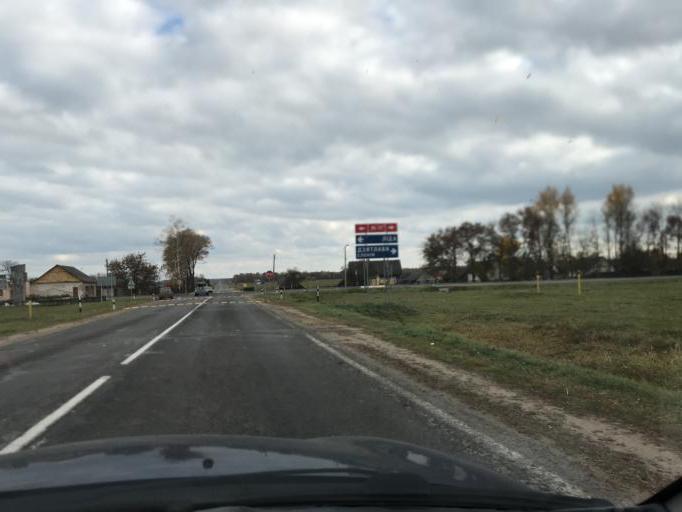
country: BY
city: Berezovka
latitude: 53.7398
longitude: 25.3720
